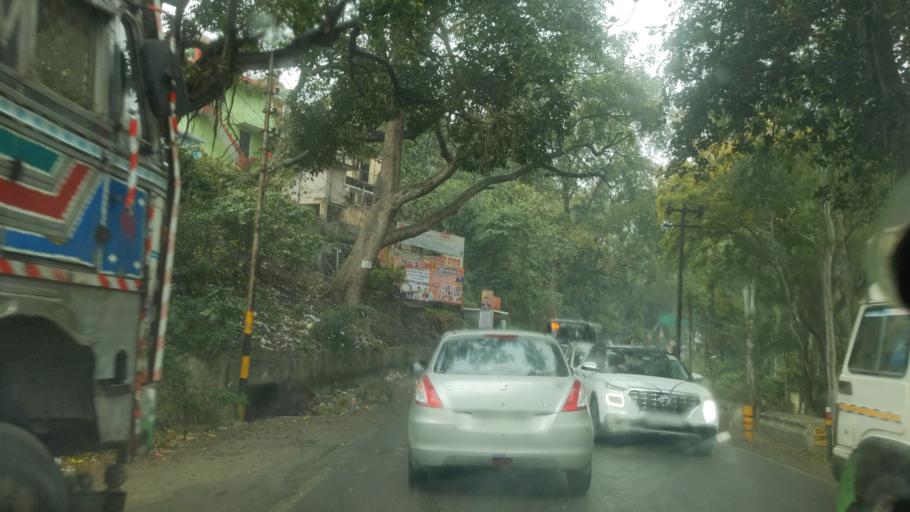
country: IN
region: Uttarakhand
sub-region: Naini Tal
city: Bhim Tal
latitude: 29.2882
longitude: 79.5473
